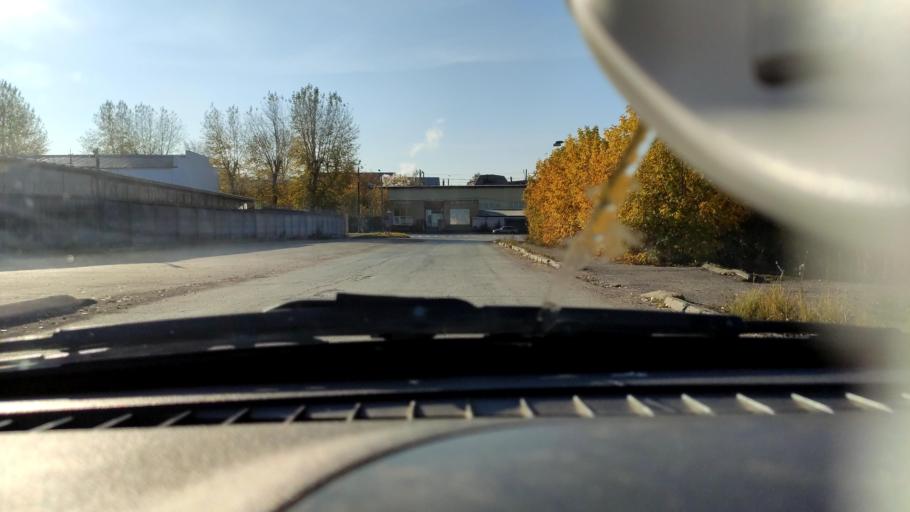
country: RU
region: Perm
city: Kondratovo
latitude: 58.0082
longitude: 56.1667
